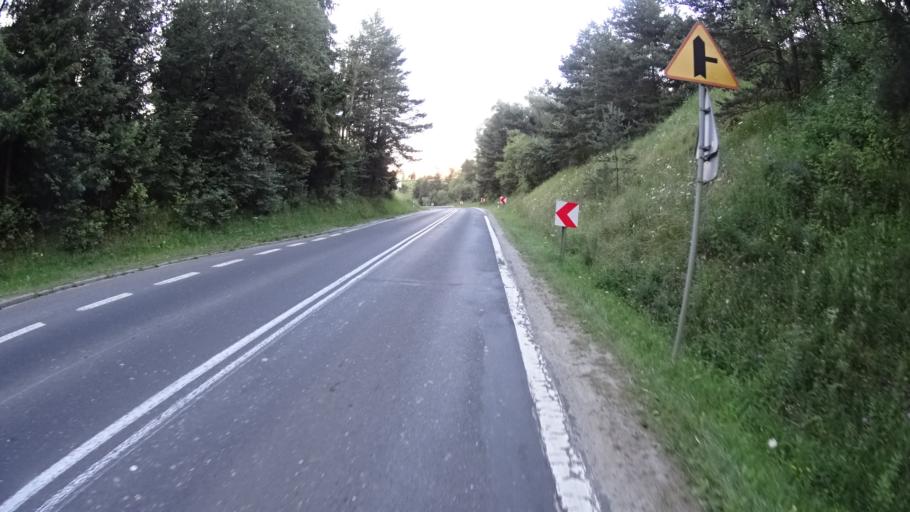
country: PL
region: Lesser Poland Voivodeship
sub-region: Powiat nowotarski
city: Frydman
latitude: 49.4675
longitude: 20.2280
